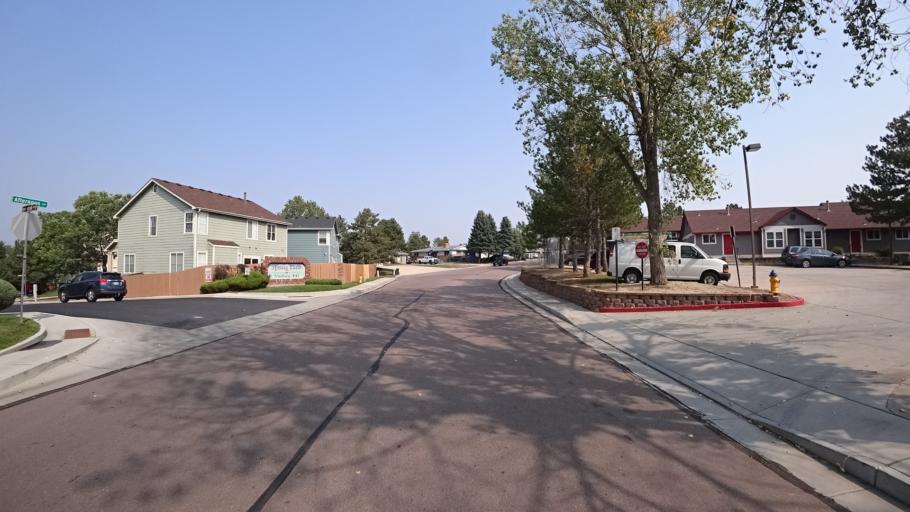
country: US
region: Colorado
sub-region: El Paso County
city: Stratmoor
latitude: 38.8182
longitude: -104.7662
